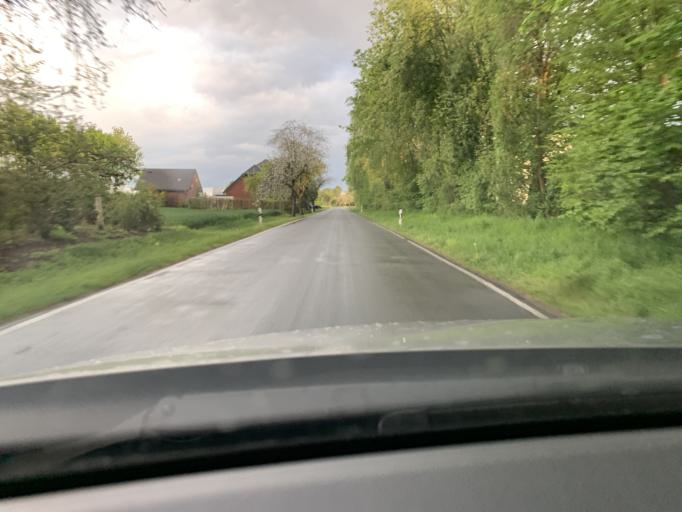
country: DE
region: North Rhine-Westphalia
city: Rietberg
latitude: 51.7757
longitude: 8.3786
